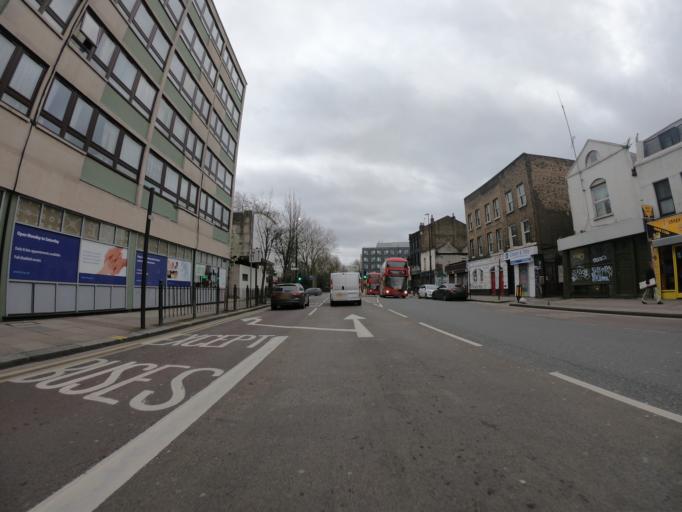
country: GB
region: England
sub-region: Greater London
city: Bethnal Green
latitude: 51.5299
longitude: -0.0560
